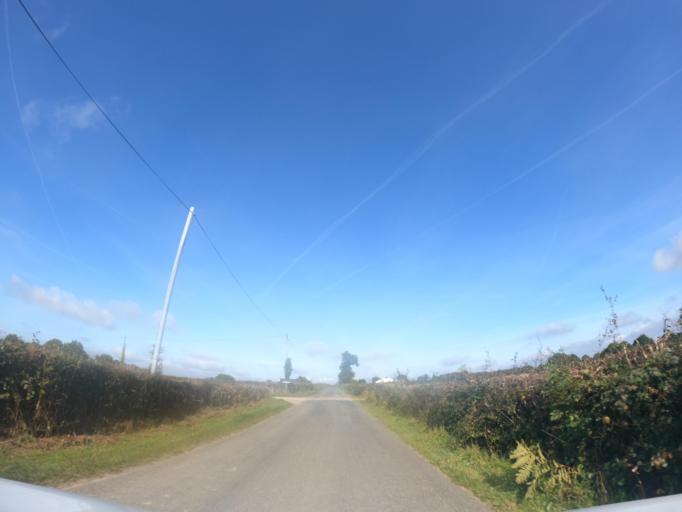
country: FR
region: Poitou-Charentes
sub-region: Departement des Deux-Sevres
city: Courlay
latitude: 46.7876
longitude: -0.5659
